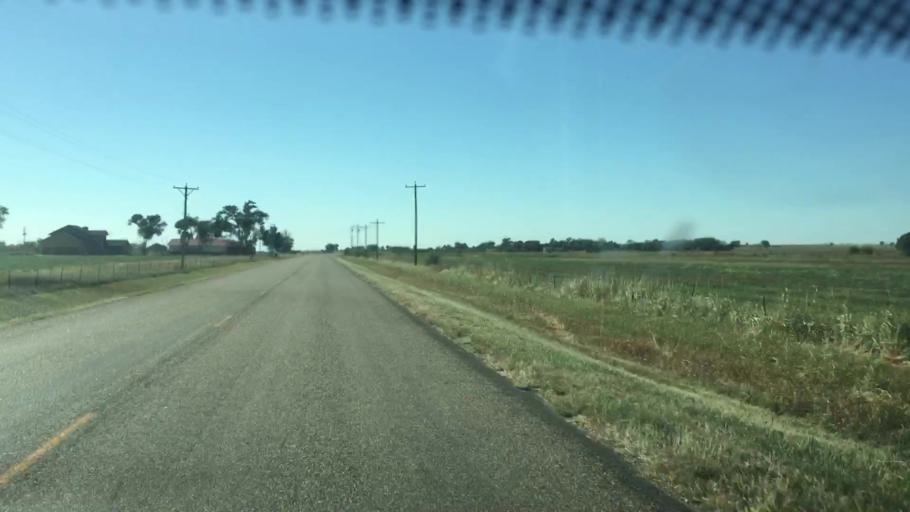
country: US
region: Colorado
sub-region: Prowers County
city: Lamar
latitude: 38.1145
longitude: -102.5633
